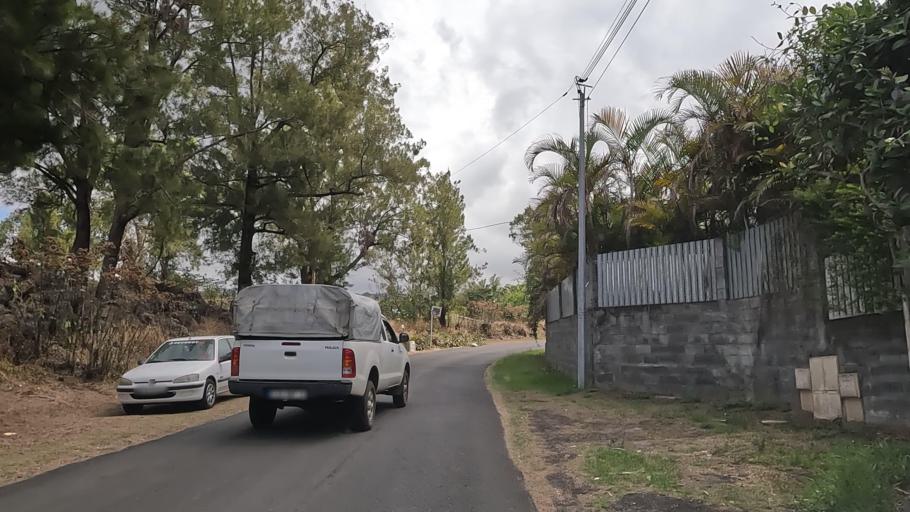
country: RE
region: Reunion
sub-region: Reunion
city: Le Tampon
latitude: -21.2608
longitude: 55.5317
